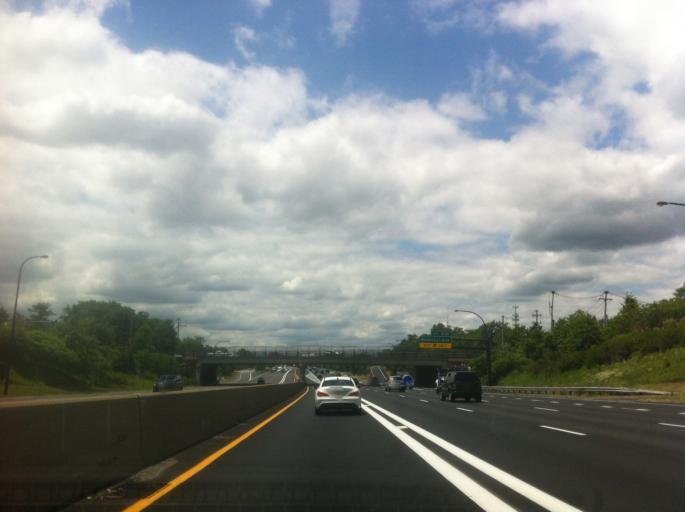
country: US
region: New York
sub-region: Nassau County
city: Syosset
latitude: 40.7981
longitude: -73.5008
